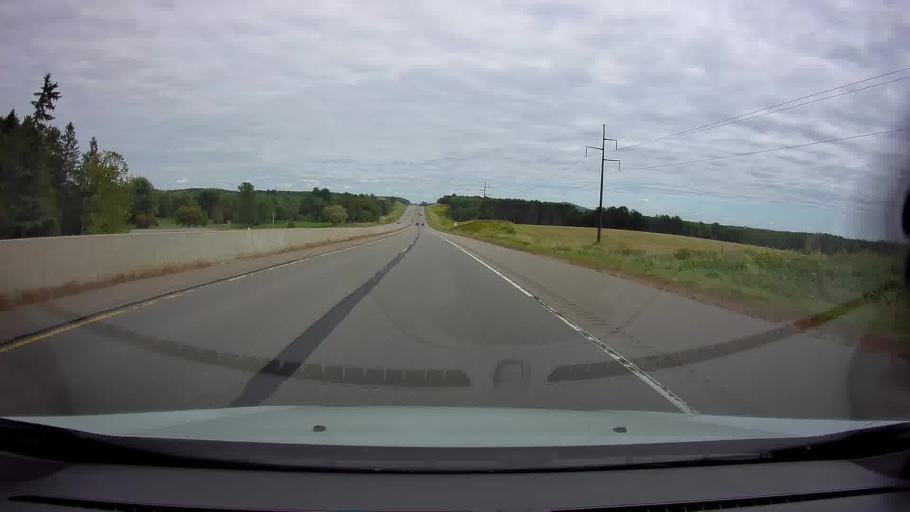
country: US
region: Wisconsin
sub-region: Marathon County
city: Marathon
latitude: 44.9440
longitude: -89.8101
